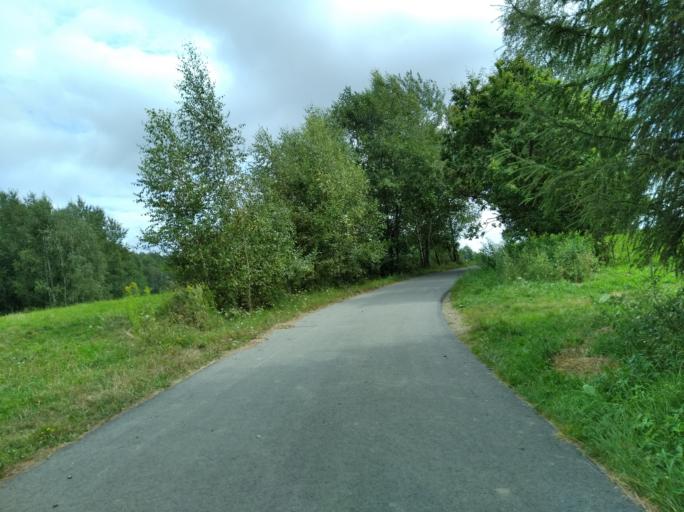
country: PL
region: Subcarpathian Voivodeship
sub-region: Powiat krosnienski
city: Odrzykon
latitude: 49.7766
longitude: 21.7268
